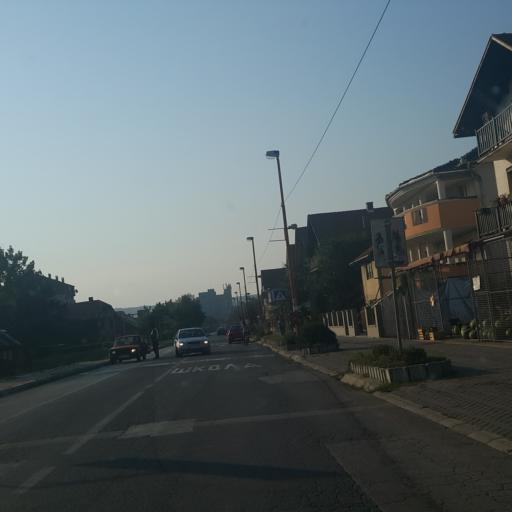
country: RS
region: Central Serbia
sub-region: Zajecarski Okrug
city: Zajecar
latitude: 43.9103
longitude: 22.2607
